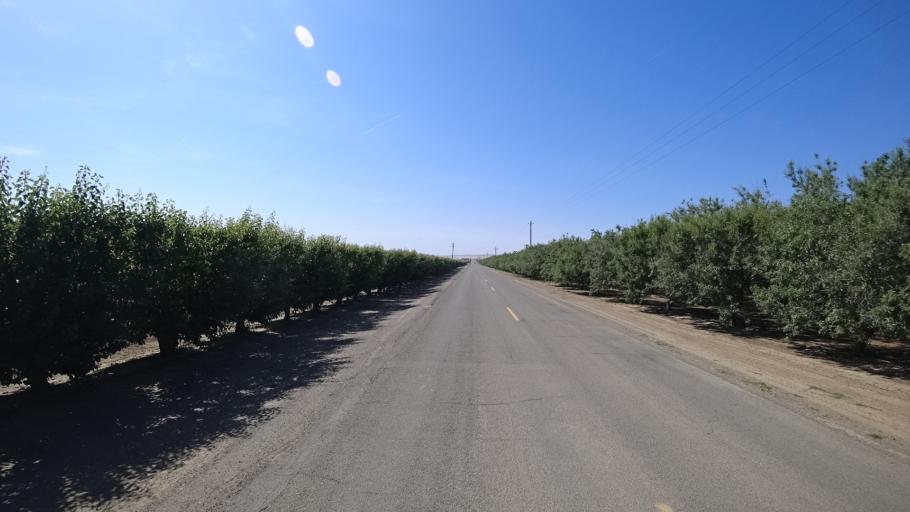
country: US
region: California
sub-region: Kings County
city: Kettleman City
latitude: 36.0633
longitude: -120.0036
